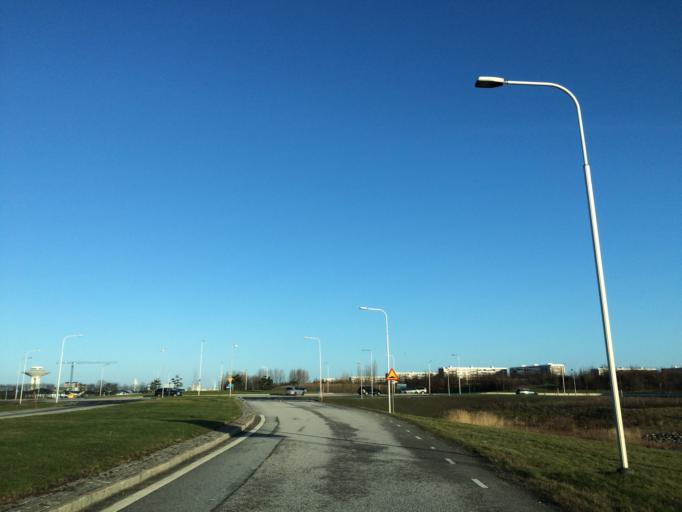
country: SE
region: Skane
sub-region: Malmo
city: Bunkeflostrand
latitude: 55.5531
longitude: 12.9833
